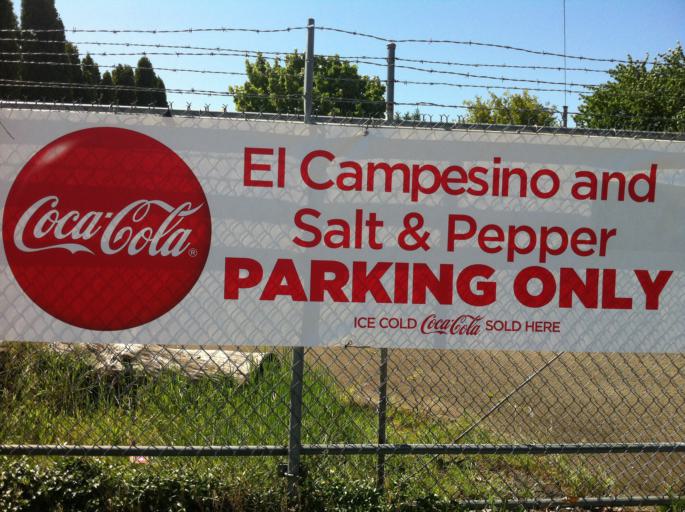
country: US
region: Oregon
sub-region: Multnomah County
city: Lents
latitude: 45.4979
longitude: -122.5948
